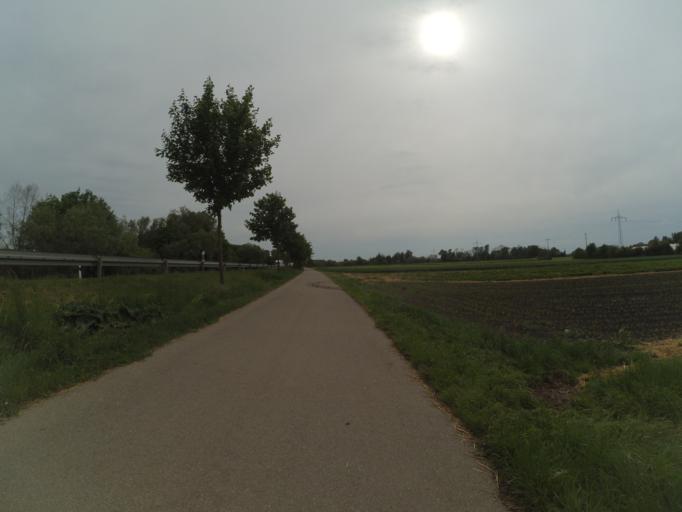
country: DE
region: Bavaria
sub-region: Swabia
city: Guenzburg
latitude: 48.4803
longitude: 10.2879
